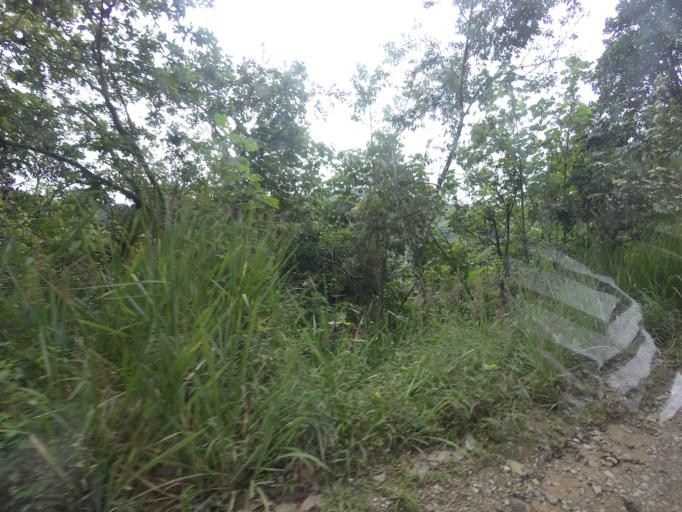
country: CO
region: Huila
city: San Agustin
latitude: 1.9295
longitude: -76.3002
